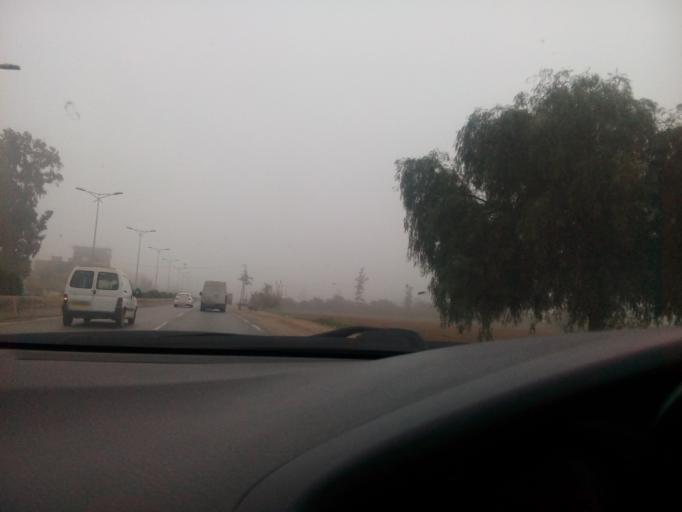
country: DZ
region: Oran
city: Bou Tlelis
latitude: 35.5744
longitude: -0.8547
